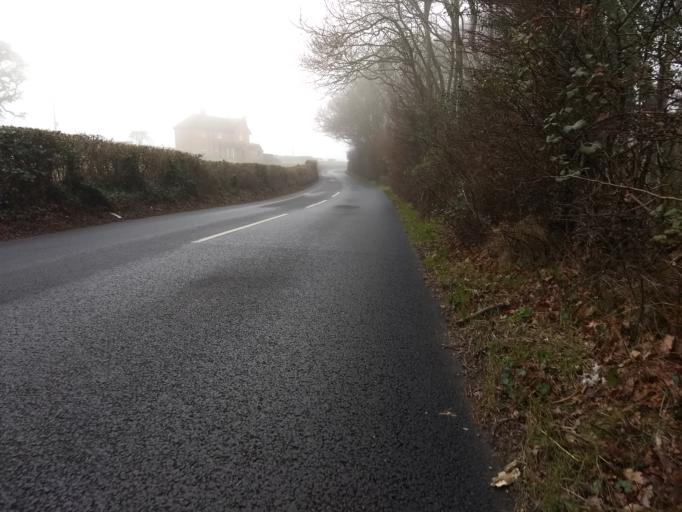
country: GB
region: England
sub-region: Isle of Wight
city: Newchurch
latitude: 50.7008
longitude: -1.2363
